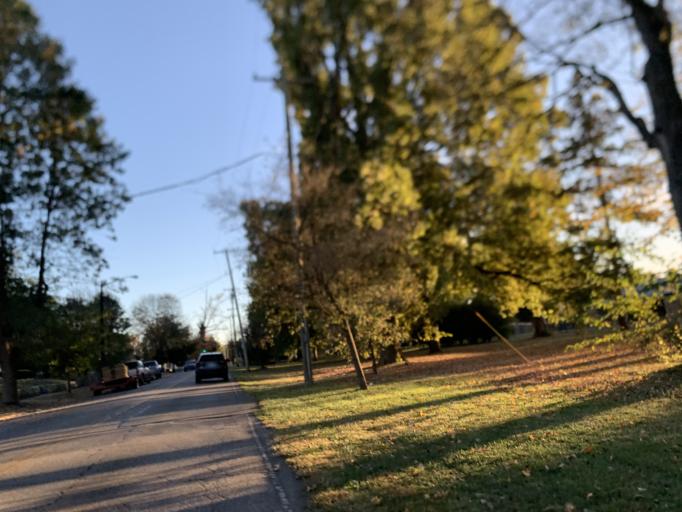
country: US
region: Indiana
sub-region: Floyd County
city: New Albany
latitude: 38.2520
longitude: -85.8269
